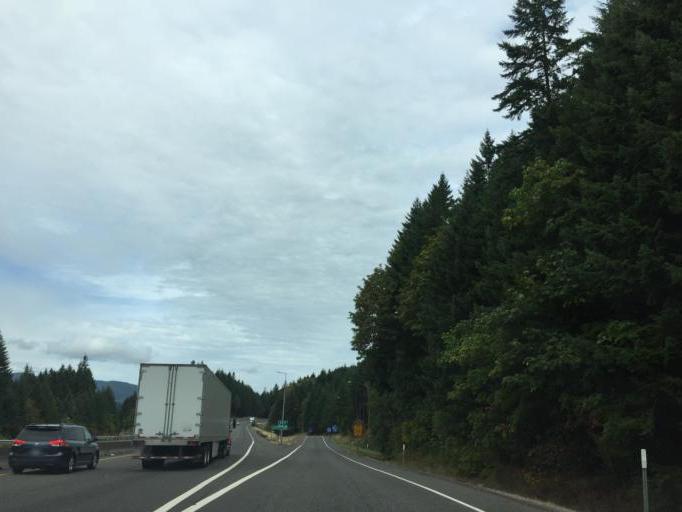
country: US
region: Oregon
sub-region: Hood River County
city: Cascade Locks
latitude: 45.6566
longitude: -121.9003
